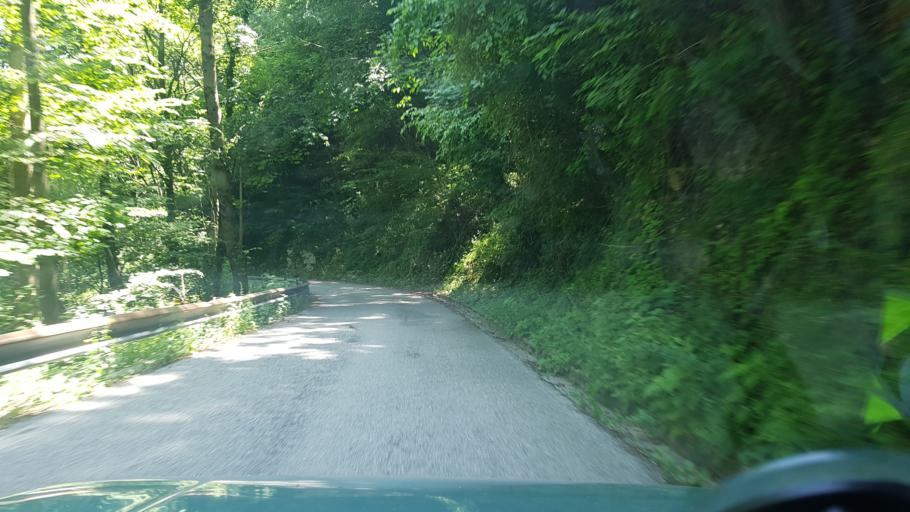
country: IT
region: Friuli Venezia Giulia
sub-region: Provincia di Udine
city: Nimis
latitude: 46.2339
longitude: 13.2762
